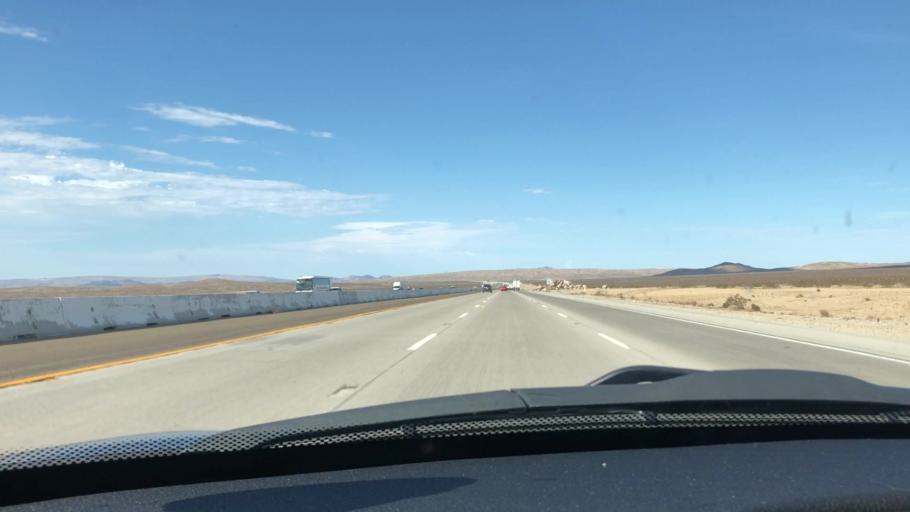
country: US
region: California
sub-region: San Bernardino County
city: Lenwood
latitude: 34.7831
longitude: -117.1292
